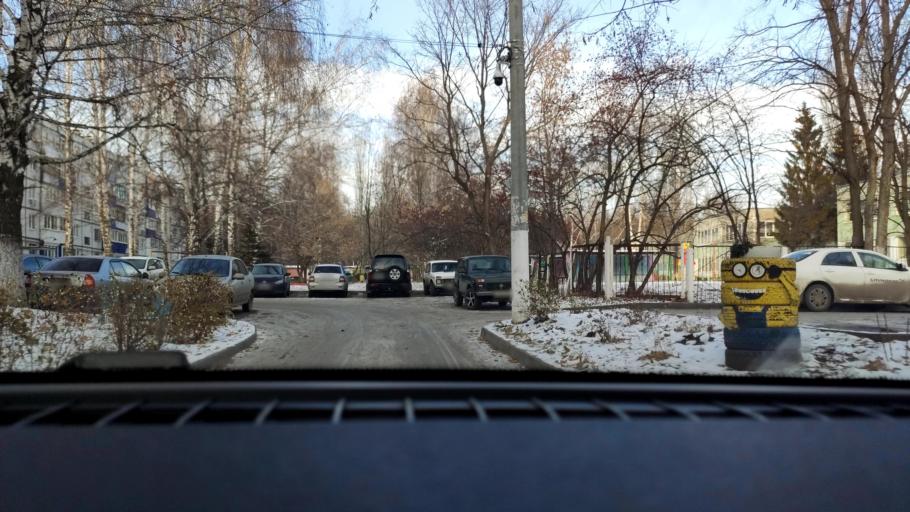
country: RU
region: Samara
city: Petra-Dubrava
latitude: 53.3024
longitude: 50.2684
